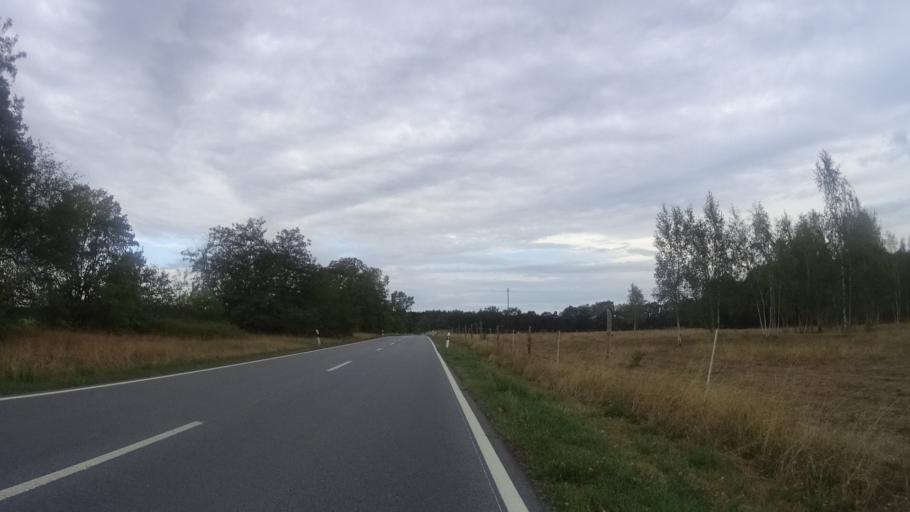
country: PL
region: Lower Silesian Voivodeship
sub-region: Powiat zgorzelecki
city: Piensk
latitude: 51.2819
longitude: 15.0261
